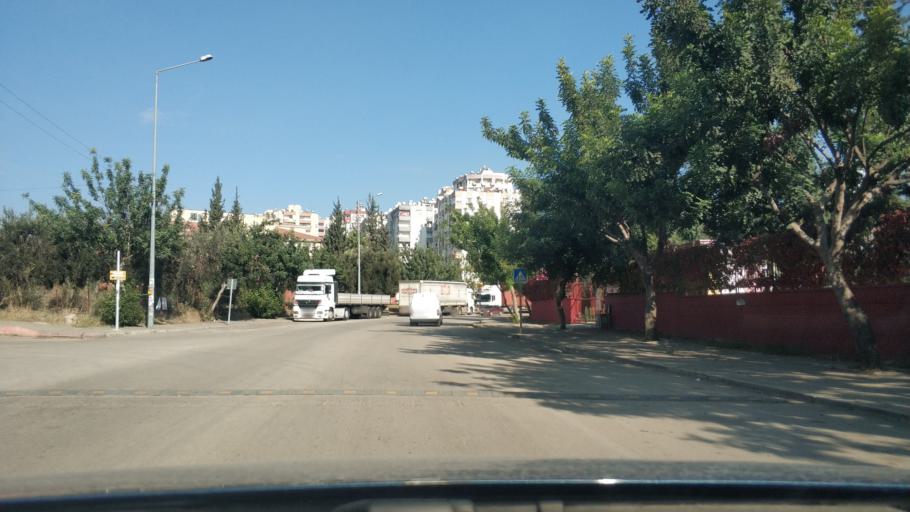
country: TR
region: Adana
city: Seyhan
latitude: 37.0215
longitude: 35.2911
